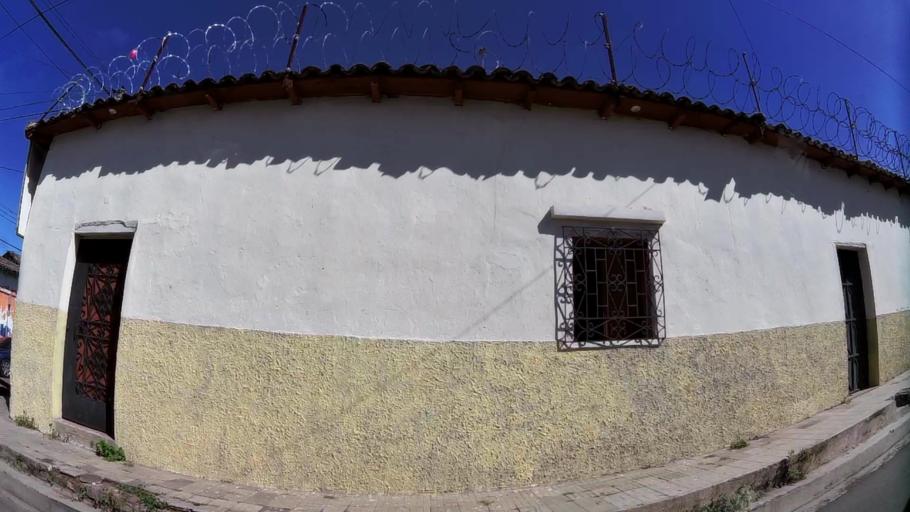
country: SV
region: Santa Ana
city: Chalchuapa
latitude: 13.9878
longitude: -89.6779
